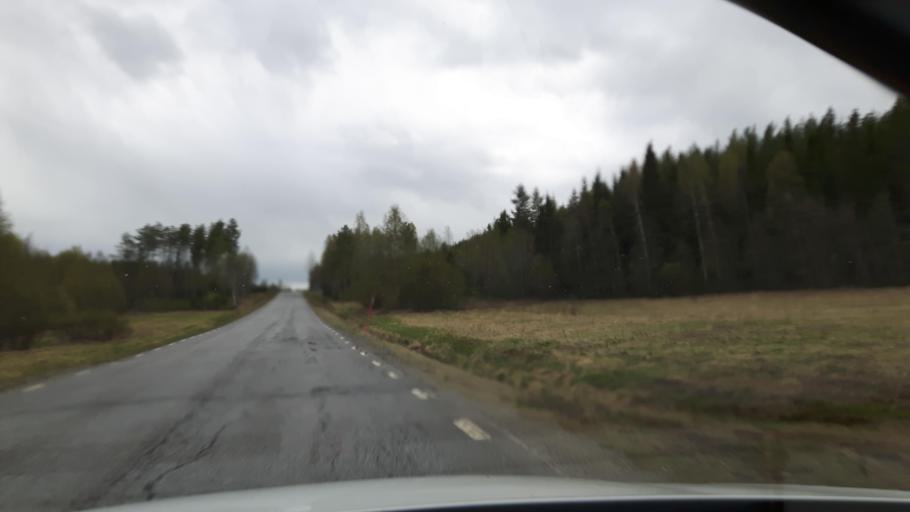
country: SE
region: Vaesterbotten
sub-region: Skelleftea Kommun
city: Burtraesk
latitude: 64.2908
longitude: 20.5236
